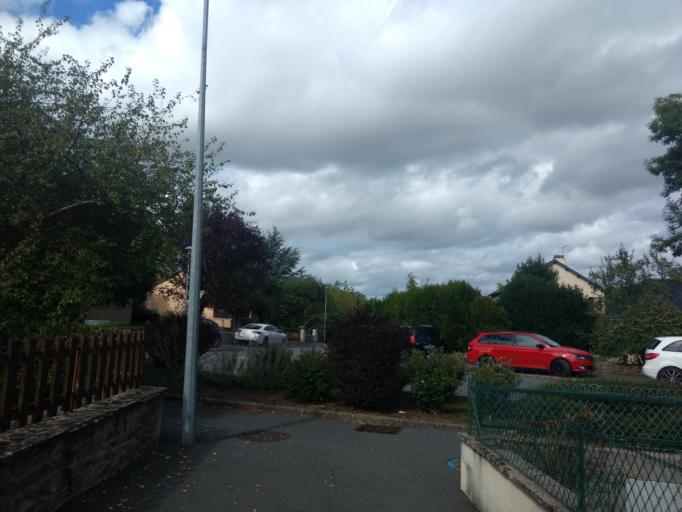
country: FR
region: Midi-Pyrenees
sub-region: Departement de l'Aveyron
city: Colombies
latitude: 44.4067
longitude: 2.2964
